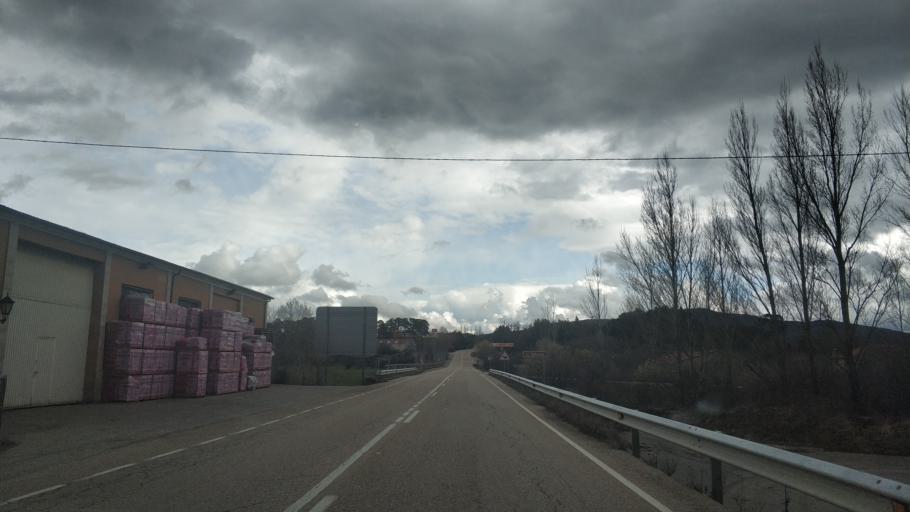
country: ES
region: Castille and Leon
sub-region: Provincia de Burgos
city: Quintanar de la Sierra
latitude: 41.9745
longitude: -3.0446
